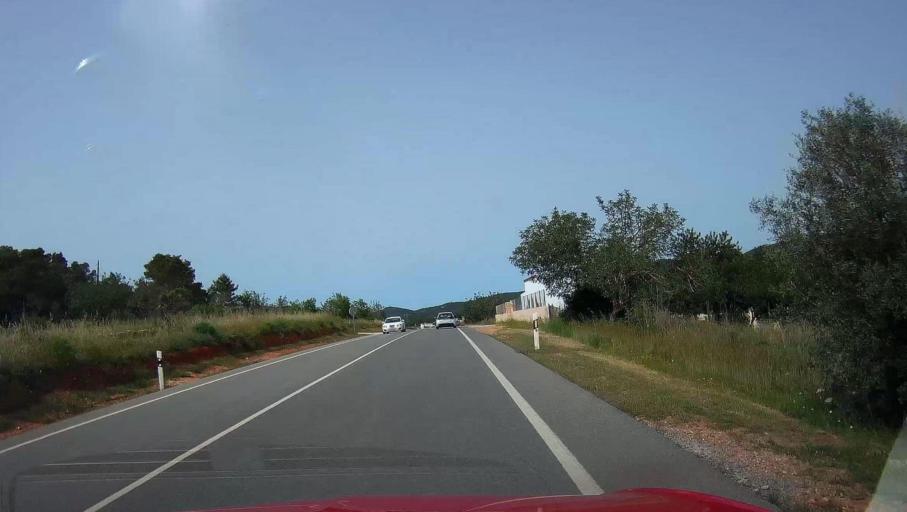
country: ES
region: Balearic Islands
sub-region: Illes Balears
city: Sant Joan de Labritja
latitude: 39.0366
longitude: 1.4914
